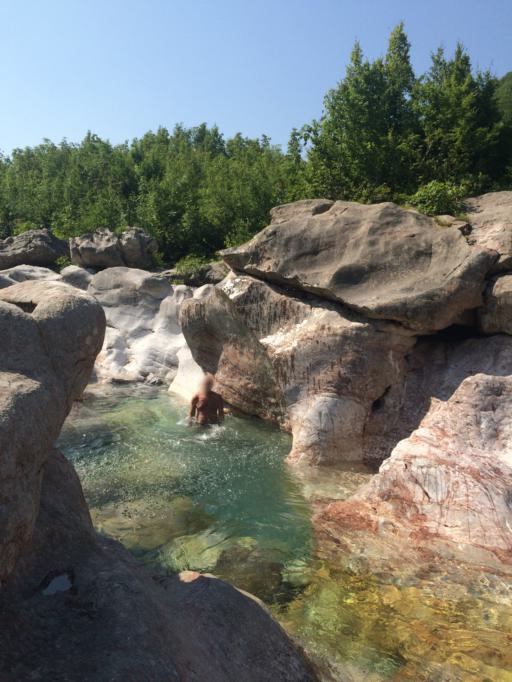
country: AL
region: Shkoder
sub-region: Rrethi i Shkodres
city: Nicaj-Shale
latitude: 42.3558
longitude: 19.7654
